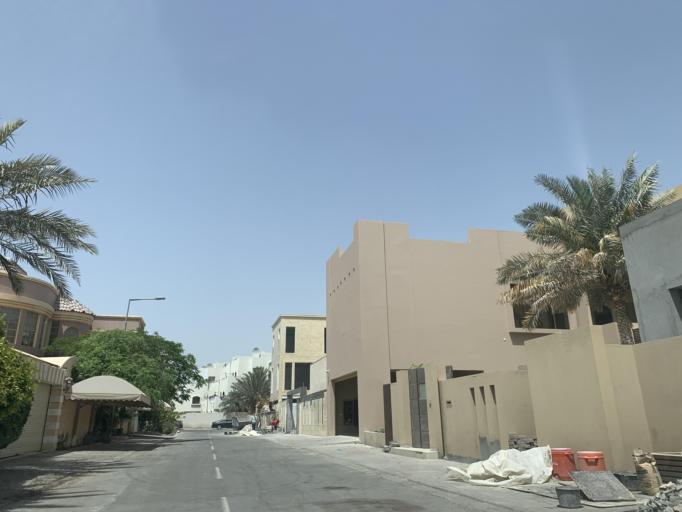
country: BH
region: Northern
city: Sitrah
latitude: 26.1565
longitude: 50.5851
